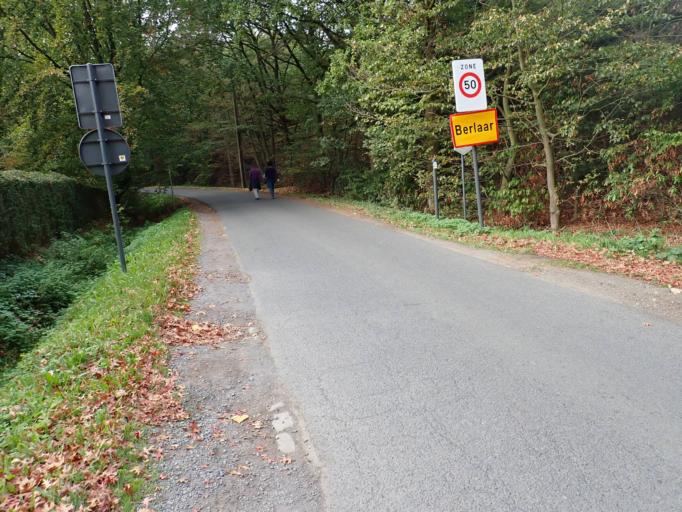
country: BE
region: Flanders
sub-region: Provincie Antwerpen
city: Berlaar
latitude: 51.1218
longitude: 4.6873
